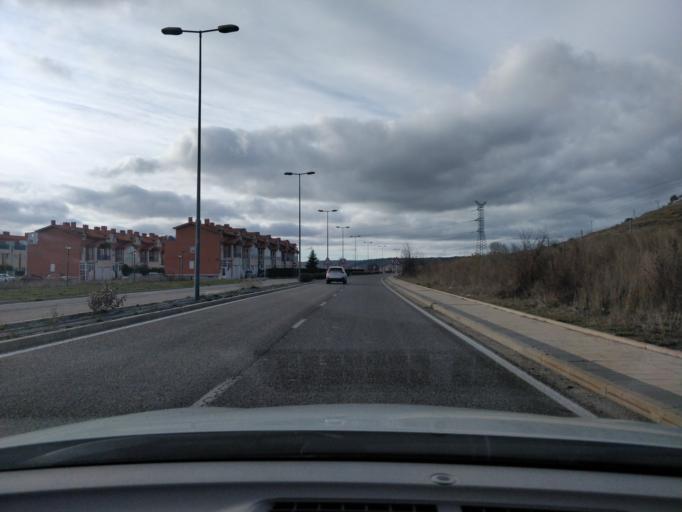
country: ES
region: Castille and Leon
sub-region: Provincia de Burgos
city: Villalbilla de Burgos
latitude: 42.3519
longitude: -3.7412
